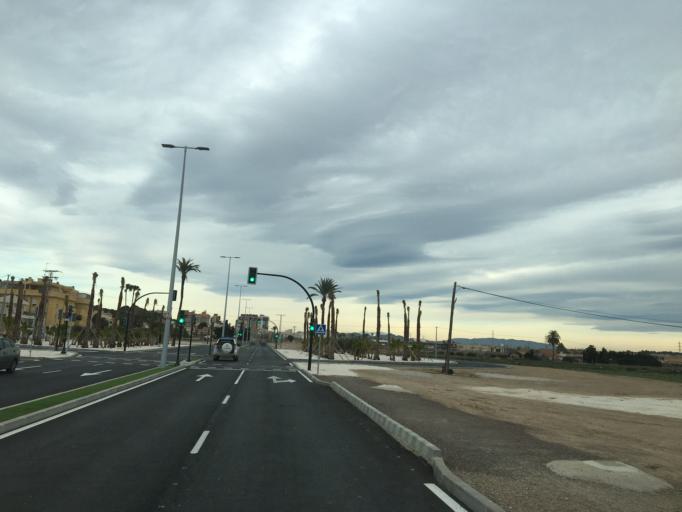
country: ES
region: Murcia
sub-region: Murcia
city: Cartagena
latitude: 37.6084
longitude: -0.9976
